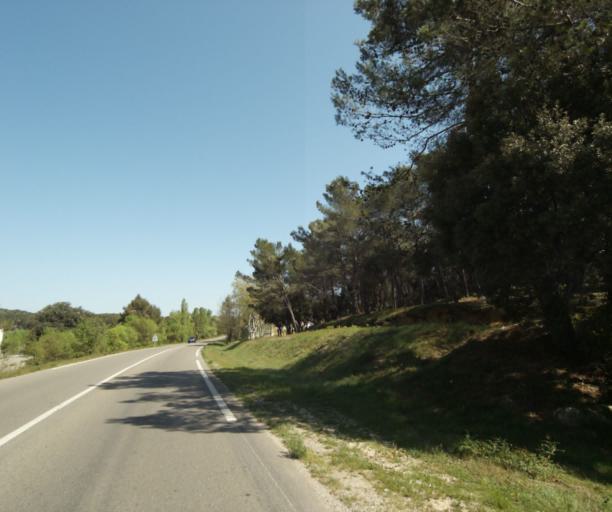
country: FR
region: Languedoc-Roussillon
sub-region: Departement de l'Herault
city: Clapiers
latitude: 43.6534
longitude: 3.8978
